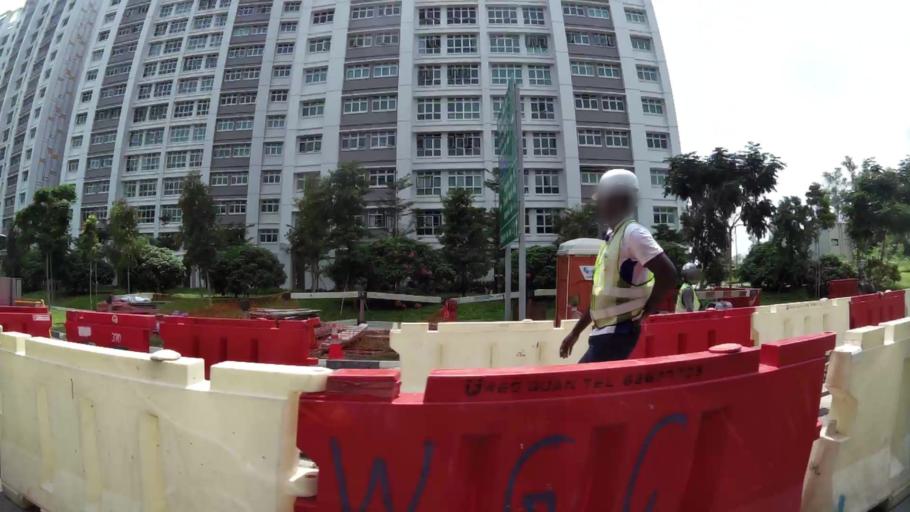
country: SG
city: Singapore
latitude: 1.3572
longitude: 103.9314
